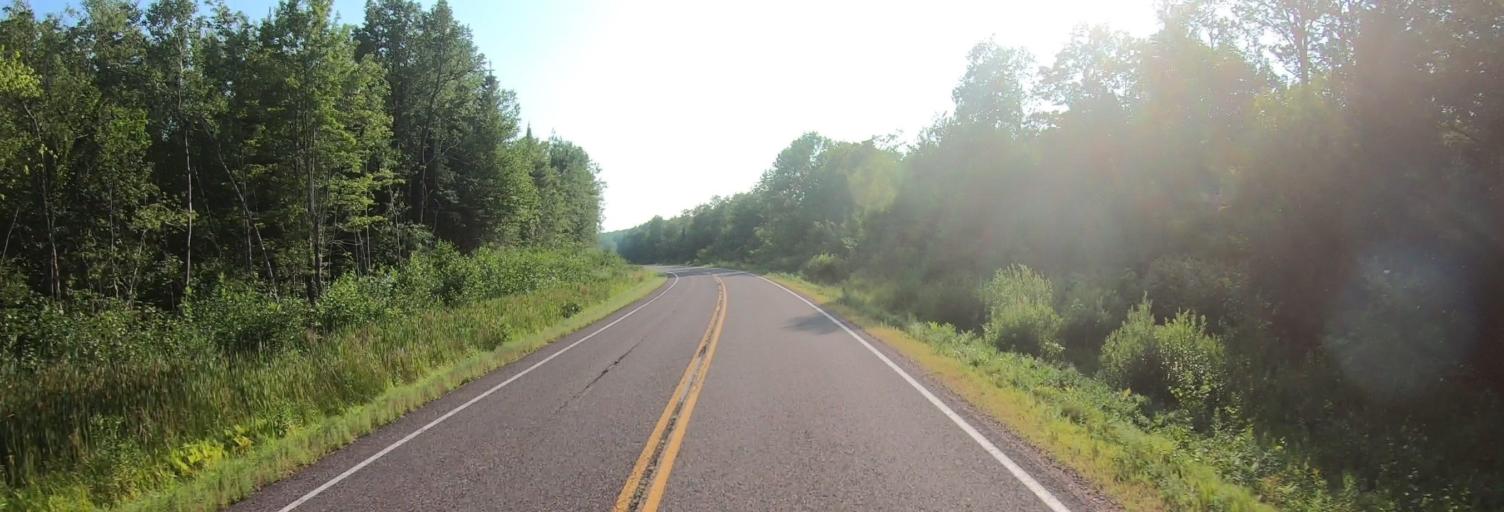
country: US
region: Wisconsin
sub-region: Ashland County
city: Ashland
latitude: 46.2984
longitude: -90.7928
